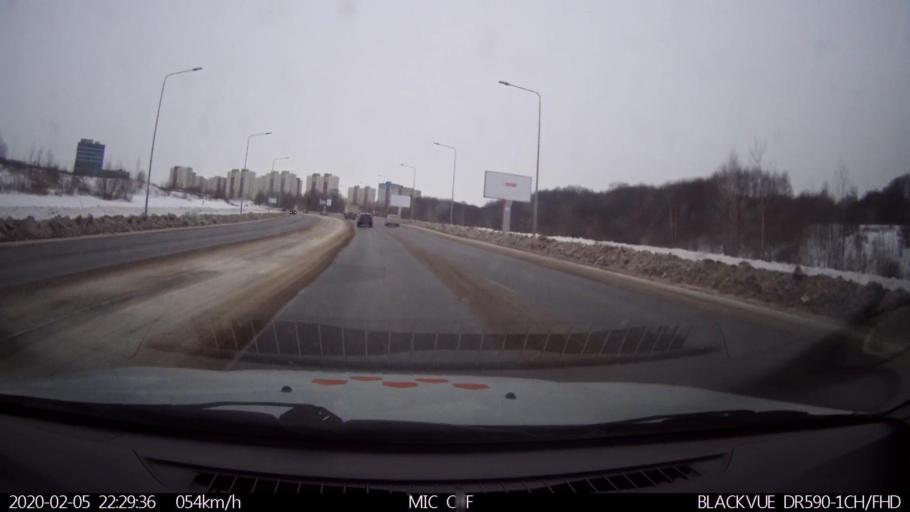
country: RU
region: Nizjnij Novgorod
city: Imeni Stepana Razina
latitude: 54.7481
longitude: 44.1466
